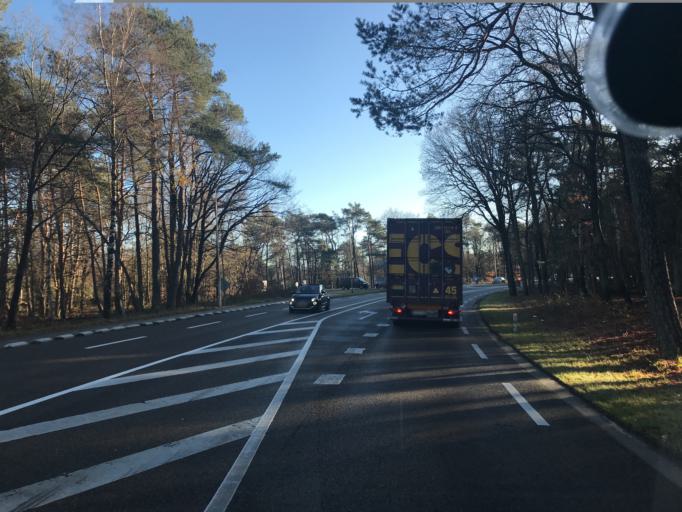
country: NL
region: Gelderland
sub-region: Gemeente Ermelo
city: Ermelo
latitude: 52.3086
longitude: 5.6814
